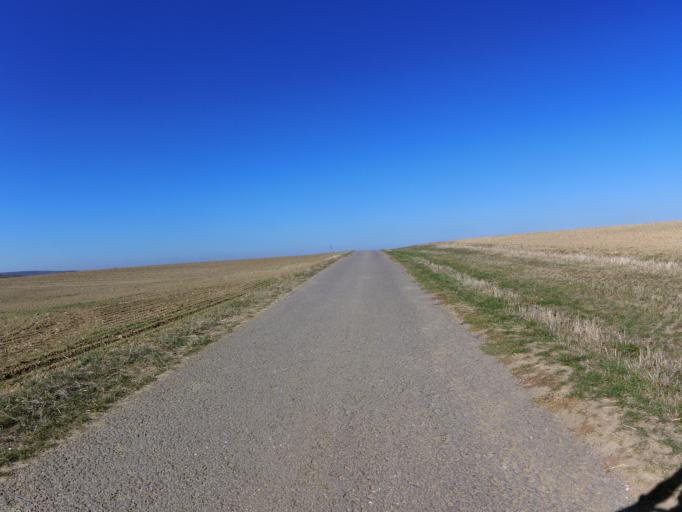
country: DE
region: Bavaria
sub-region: Regierungsbezirk Unterfranken
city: Eibelstadt
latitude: 49.7099
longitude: 9.9722
